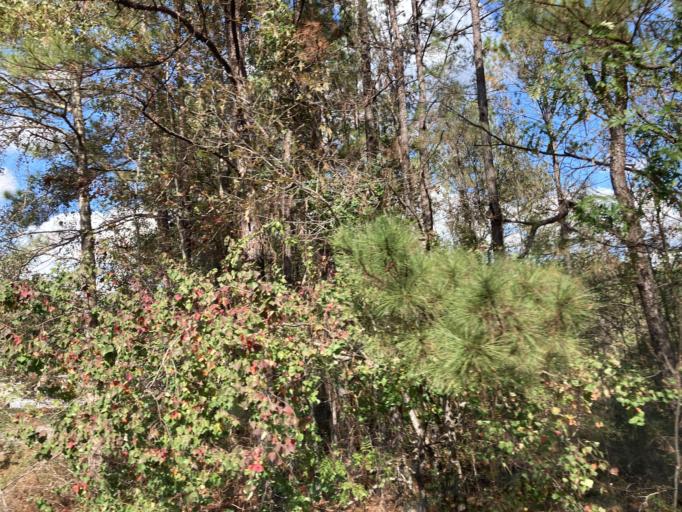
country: US
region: Mississippi
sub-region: Lamar County
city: West Hattiesburg
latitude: 31.2675
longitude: -89.4000
